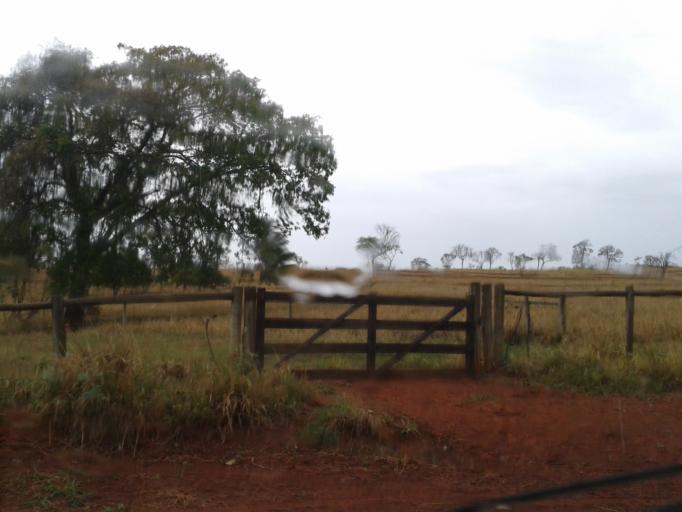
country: BR
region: Minas Gerais
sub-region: Campina Verde
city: Campina Verde
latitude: -19.3461
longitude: -49.5491
